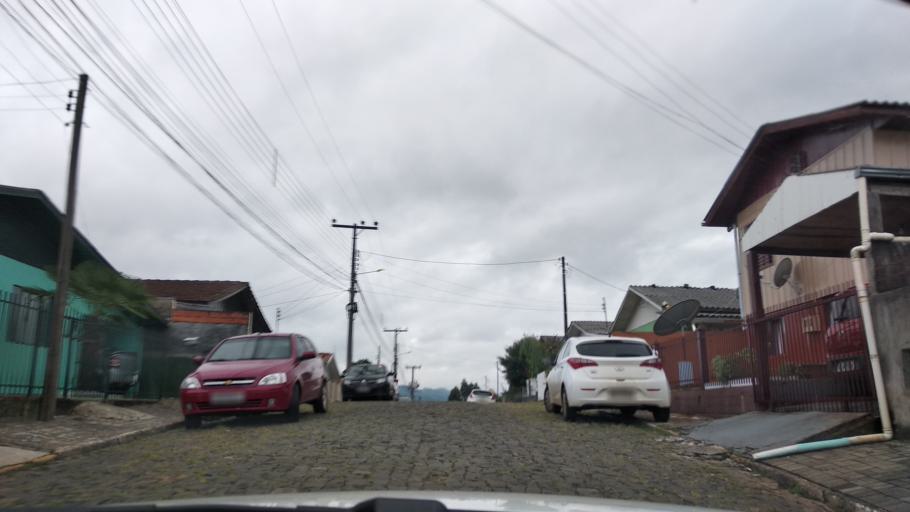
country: BR
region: Santa Catarina
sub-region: Videira
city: Videira
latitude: -26.9875
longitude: -51.1752
